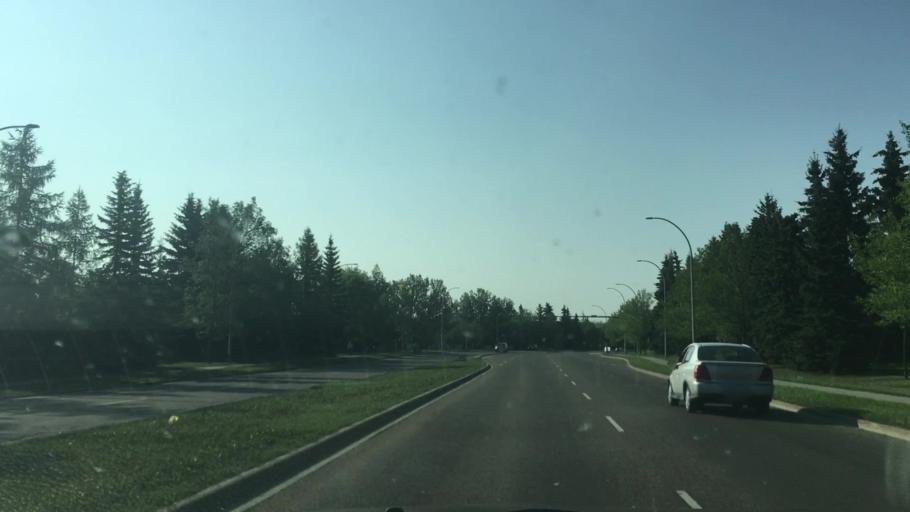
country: CA
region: Alberta
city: Edmonton
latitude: 53.4575
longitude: -113.5360
